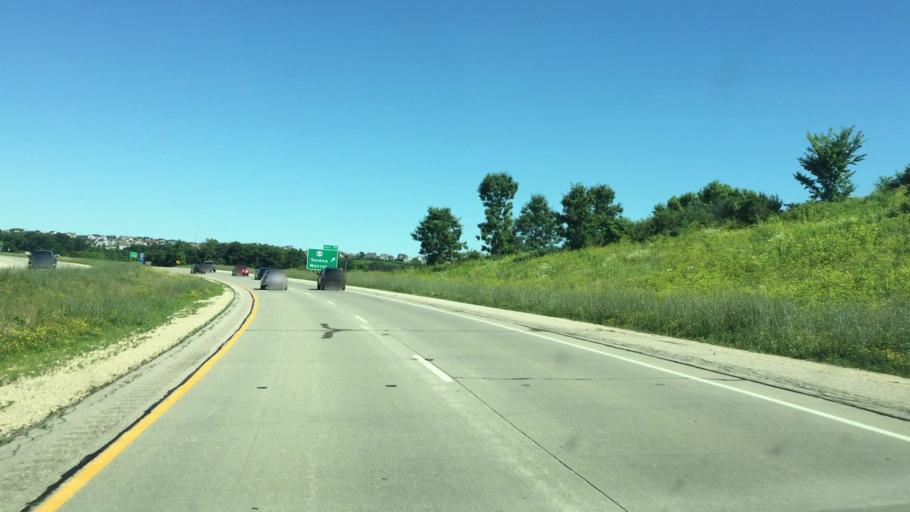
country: US
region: Wisconsin
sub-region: Dane County
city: Verona
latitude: 42.9758
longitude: -89.5537
